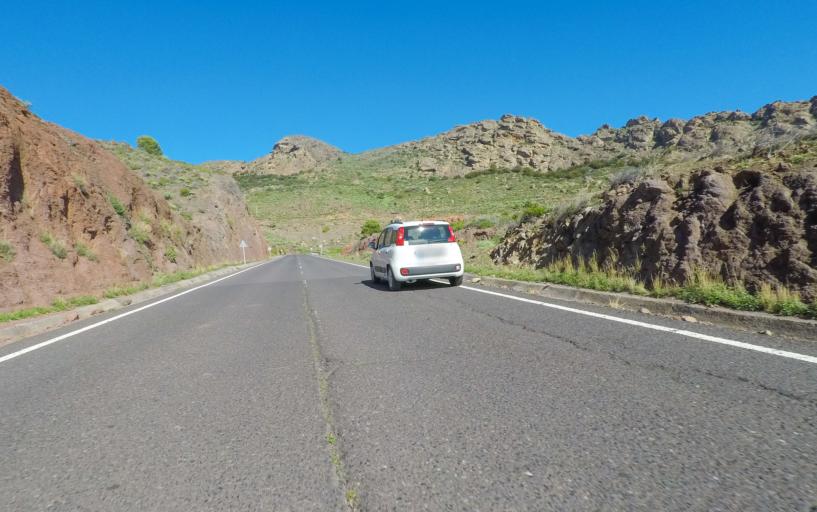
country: ES
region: Canary Islands
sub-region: Provincia de Santa Cruz de Tenerife
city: Alajero
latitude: 28.0790
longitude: -17.2014
